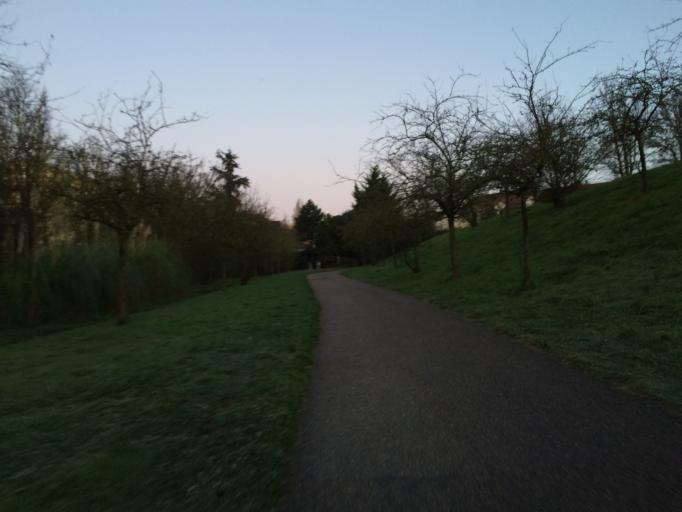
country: FR
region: Ile-de-France
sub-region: Departement de l'Essonne
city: Verrieres-le-Buisson
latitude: 48.7459
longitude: 2.2777
